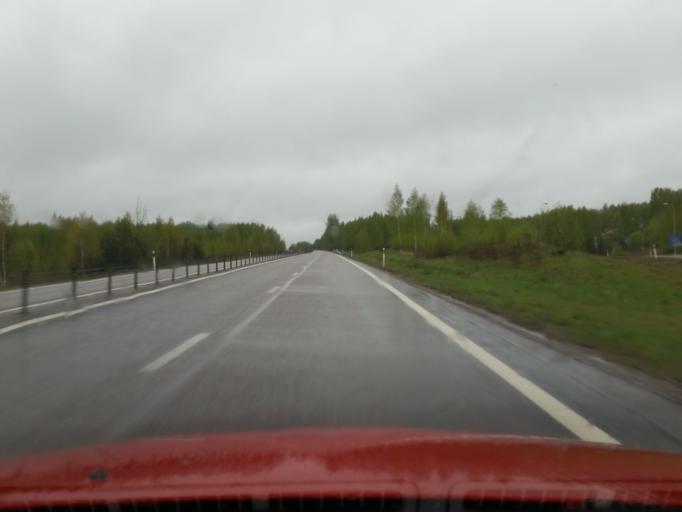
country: SE
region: Dalarna
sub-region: Borlange Kommun
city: Ornas
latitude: 60.4392
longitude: 15.5078
